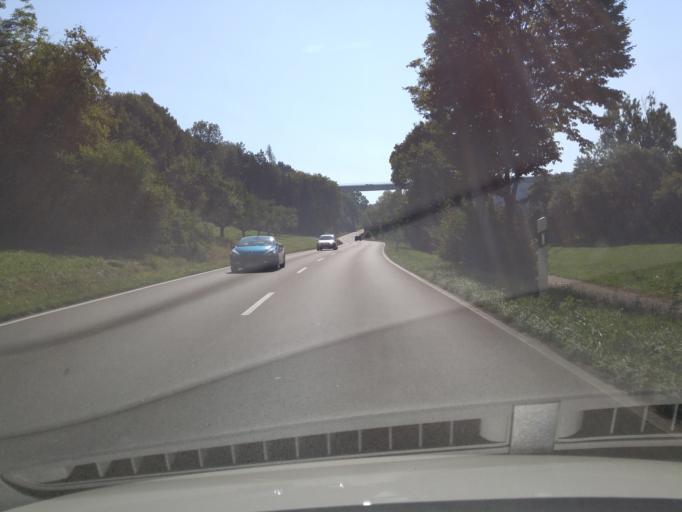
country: DE
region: Baden-Wuerttemberg
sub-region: Regierungsbezirk Stuttgart
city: Schlaitdorf
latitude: 48.6235
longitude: 9.2179
